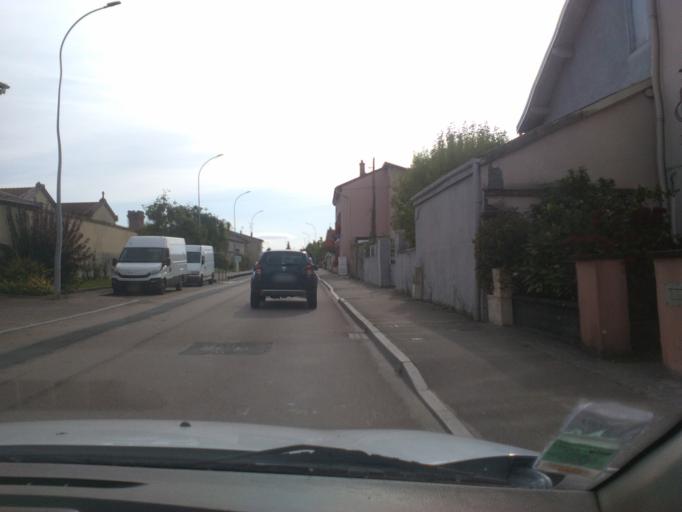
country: FR
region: Lorraine
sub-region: Departement des Vosges
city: Rambervillers
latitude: 48.3446
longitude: 6.6405
